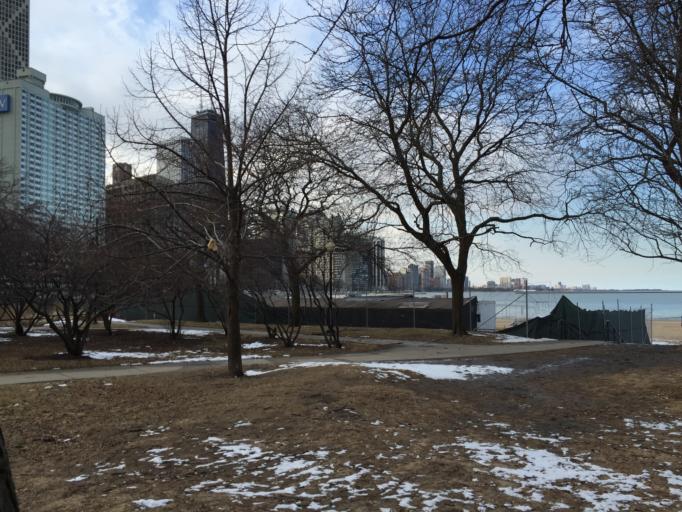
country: US
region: Illinois
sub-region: Cook County
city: Chicago
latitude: 41.8928
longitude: -87.6123
